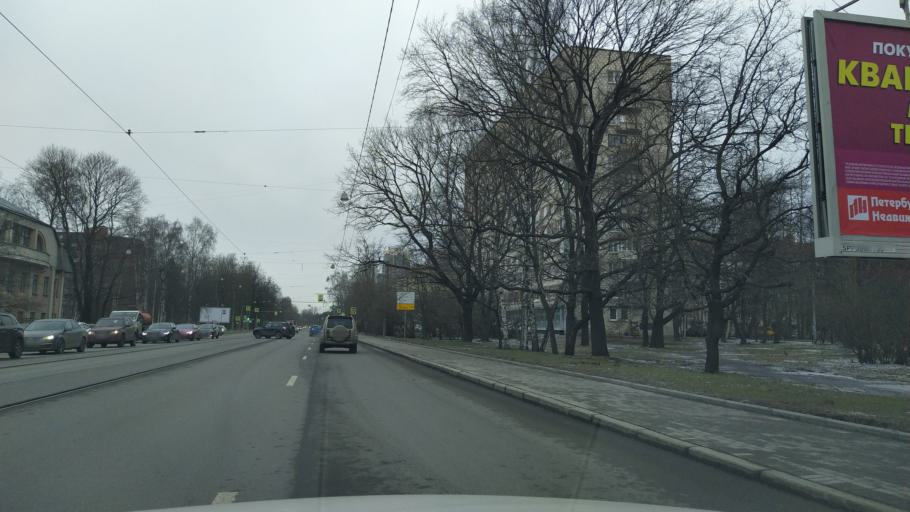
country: RU
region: Leningrad
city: Udel'naya
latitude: 60.0193
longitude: 30.3215
